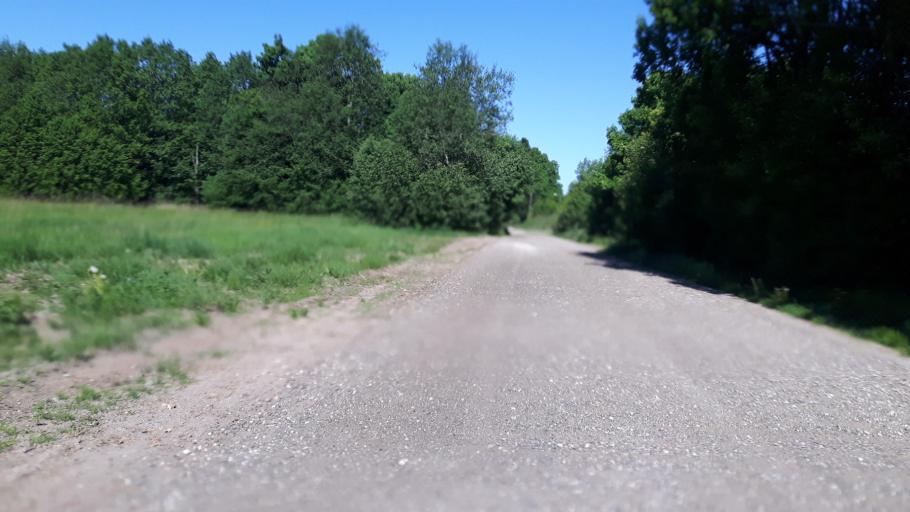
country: EE
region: Harju
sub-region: Loksa linn
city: Loksa
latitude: 59.5762
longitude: 25.7291
